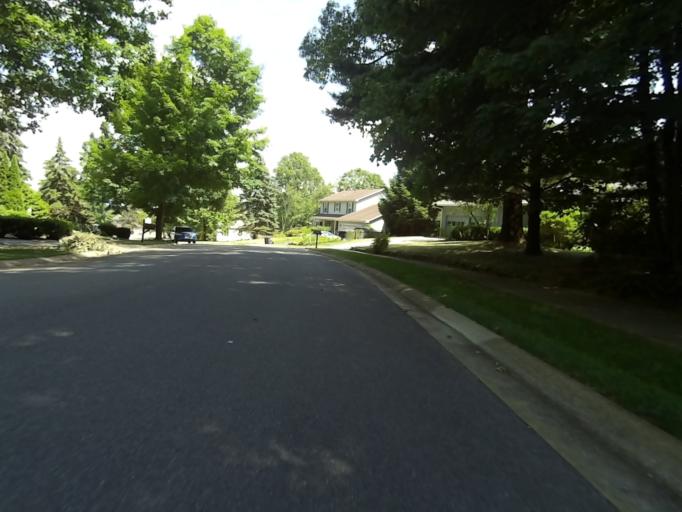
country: US
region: Pennsylvania
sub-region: Centre County
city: Park Forest Village
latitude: 40.7951
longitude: -77.9072
